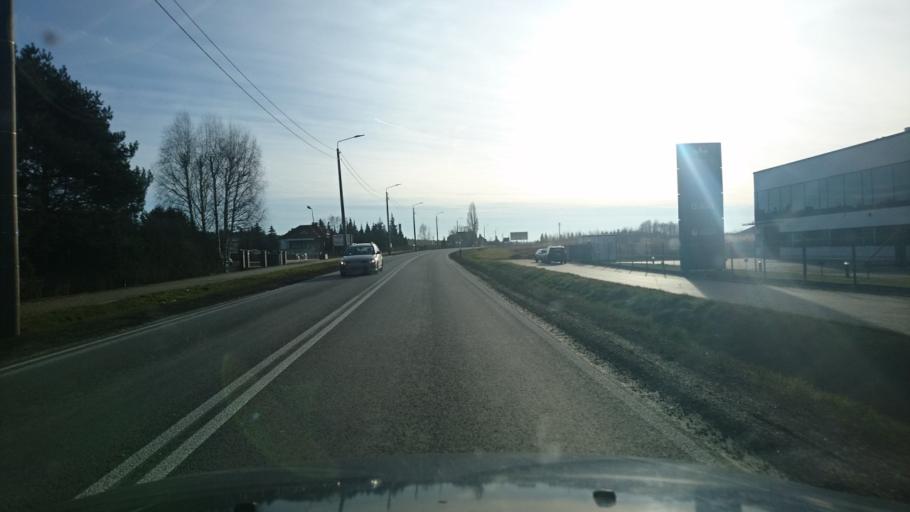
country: PL
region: Greater Poland Voivodeship
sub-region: Powiat ostrzeszowski
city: Ostrzeszow
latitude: 51.4434
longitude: 17.9129
